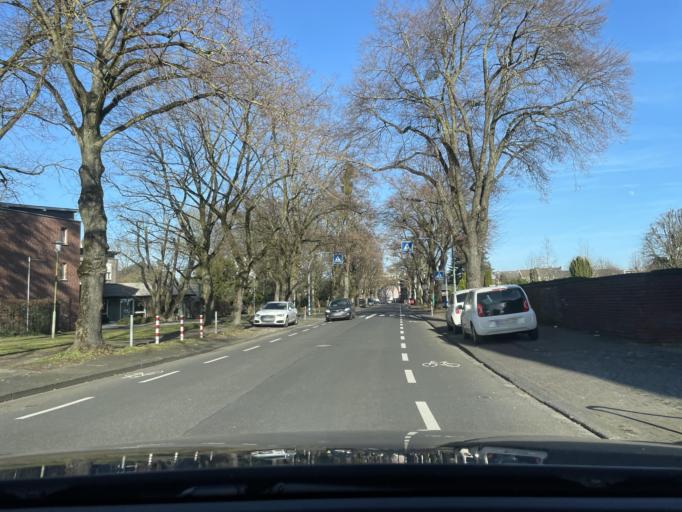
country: DE
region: North Rhine-Westphalia
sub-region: Regierungsbezirk Dusseldorf
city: Monchengladbach
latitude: 51.2221
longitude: 6.4711
